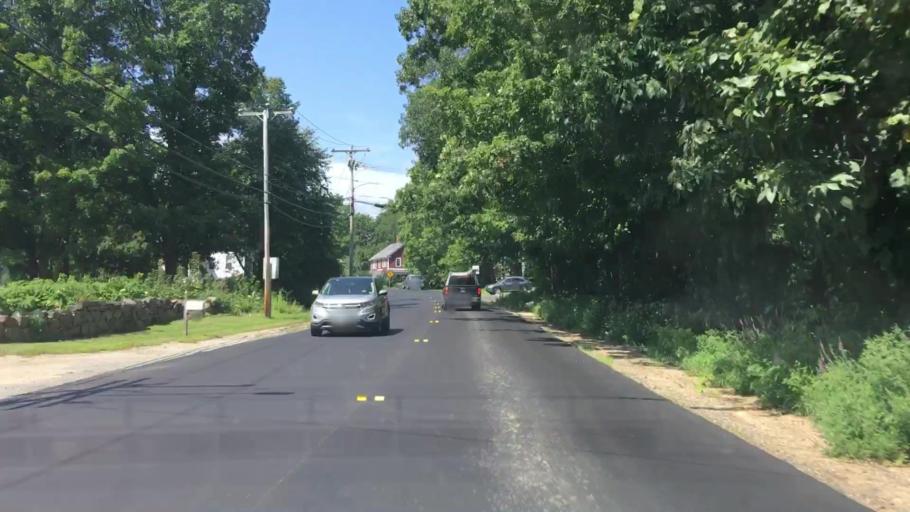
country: US
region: New Hampshire
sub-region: Rockingham County
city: Hampstead
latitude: 42.8841
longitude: -71.1902
